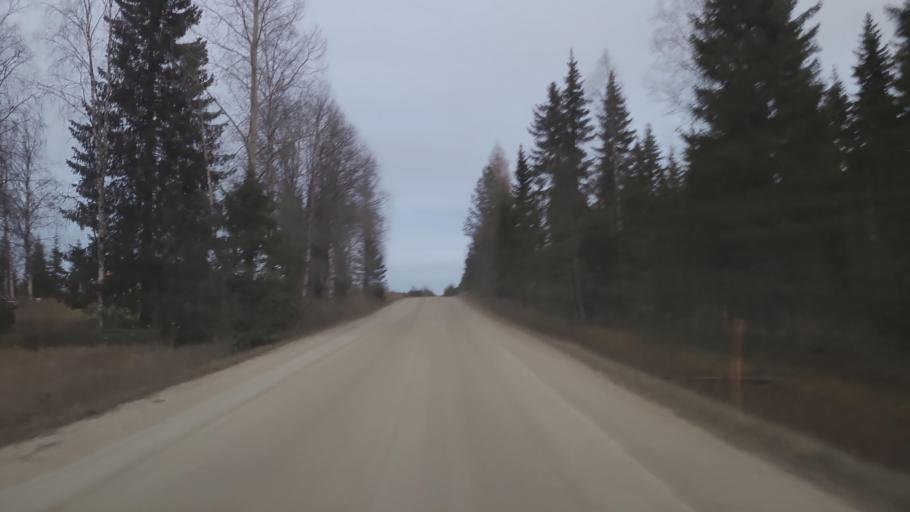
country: FI
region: Lapland
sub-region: Kemi-Tornio
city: Tervola
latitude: 66.0724
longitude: 24.8640
